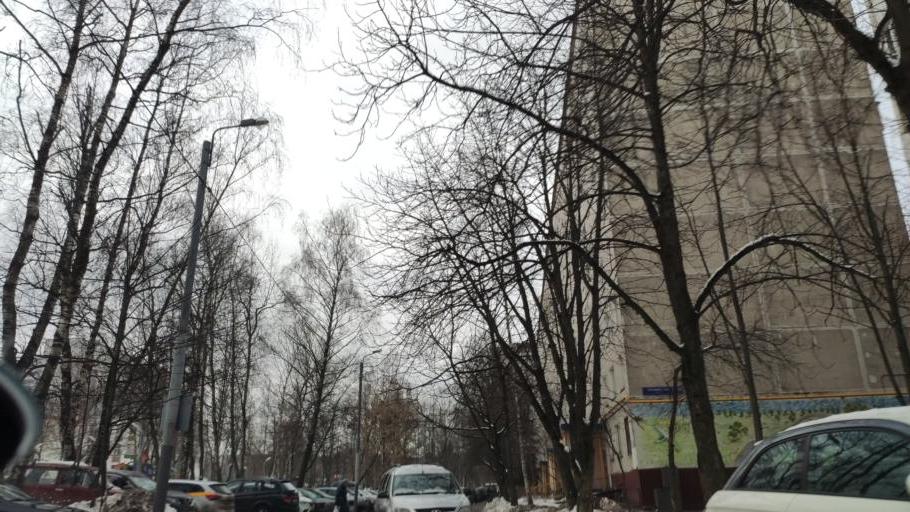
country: RU
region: Moscow
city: Tyoply Stan
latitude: 55.6212
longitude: 37.4902
